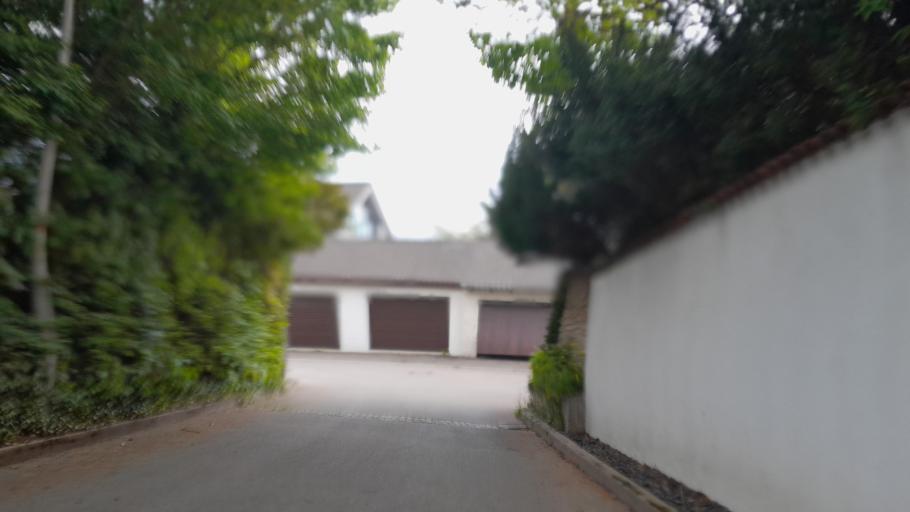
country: DE
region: Baden-Wuerttemberg
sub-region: Regierungsbezirk Stuttgart
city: Goeppingen
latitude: 48.7134
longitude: 9.6539
